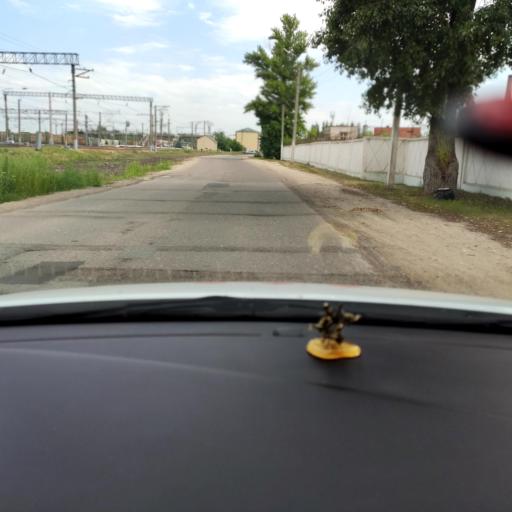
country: RU
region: Tatarstan
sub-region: Zelenodol'skiy Rayon
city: Zelenodolsk
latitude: 55.8413
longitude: 48.5551
